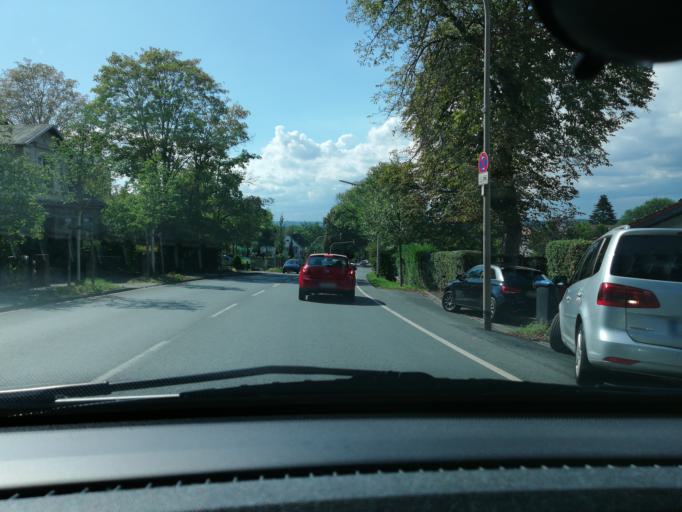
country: DE
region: North Rhine-Westphalia
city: Witten
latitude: 51.4364
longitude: 7.3769
